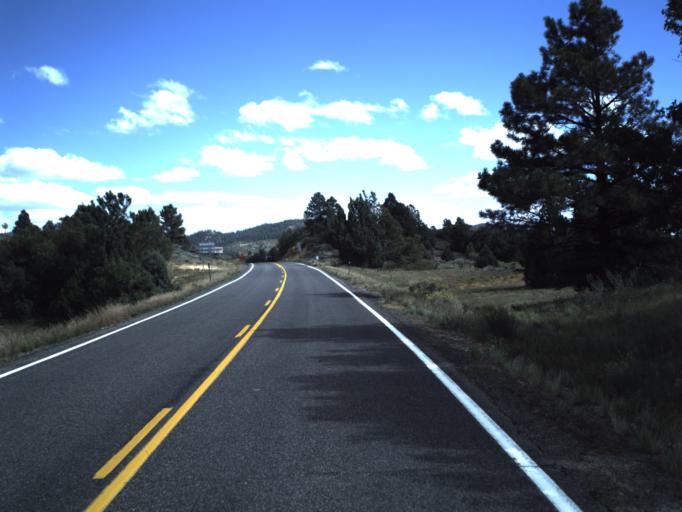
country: US
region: Utah
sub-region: Garfield County
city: Panguitch
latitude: 37.4900
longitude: -112.5191
